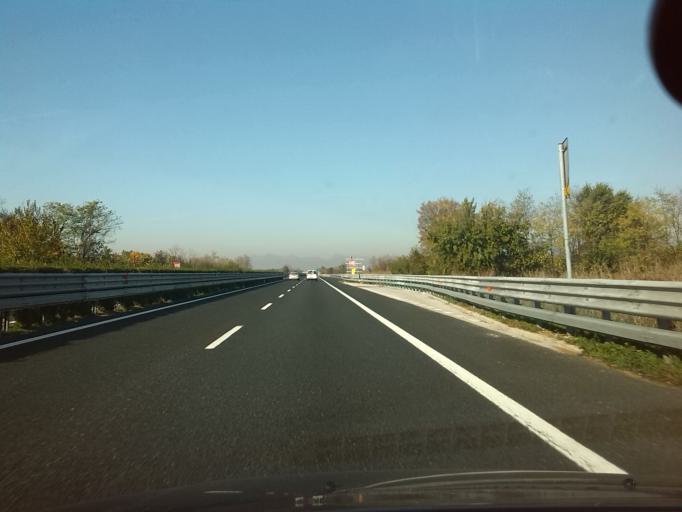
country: IT
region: Friuli Venezia Giulia
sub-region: Provincia di Udine
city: Zugliano-Terenzano-Cargnacco
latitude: 45.9885
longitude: 13.2382
